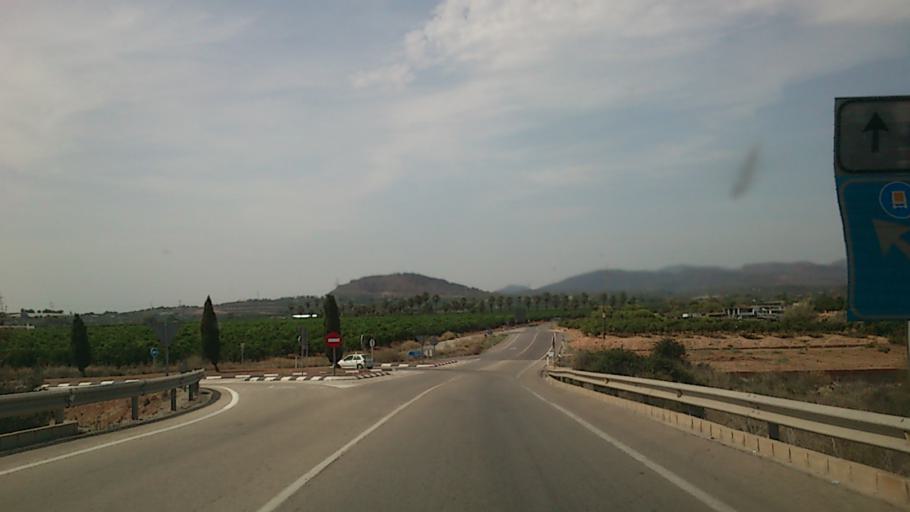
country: ES
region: Valencia
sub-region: Provincia de Valencia
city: Museros
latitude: 39.6096
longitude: -0.3453
